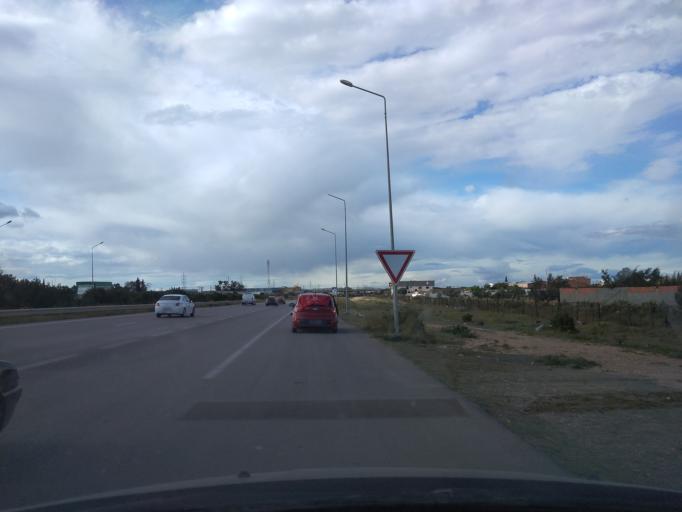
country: TN
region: Susah
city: Masakin
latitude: 35.7137
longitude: 10.5572
